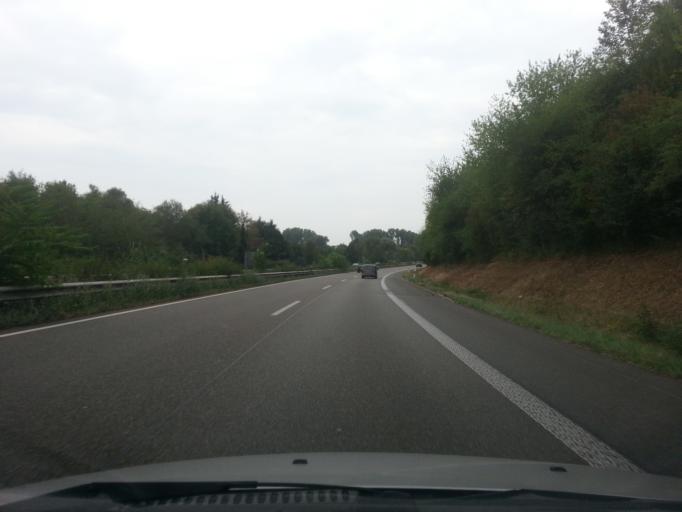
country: DE
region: Rheinland-Pfalz
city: Bornheim
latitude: 49.2085
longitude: 8.1474
